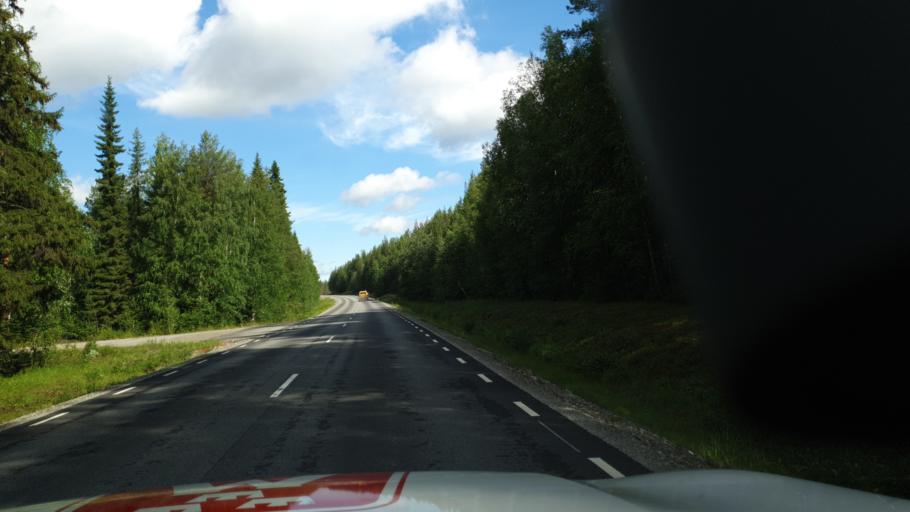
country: SE
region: Vaesterbotten
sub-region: Norsjo Kommun
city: Norsjoe
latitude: 64.6082
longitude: 19.2956
